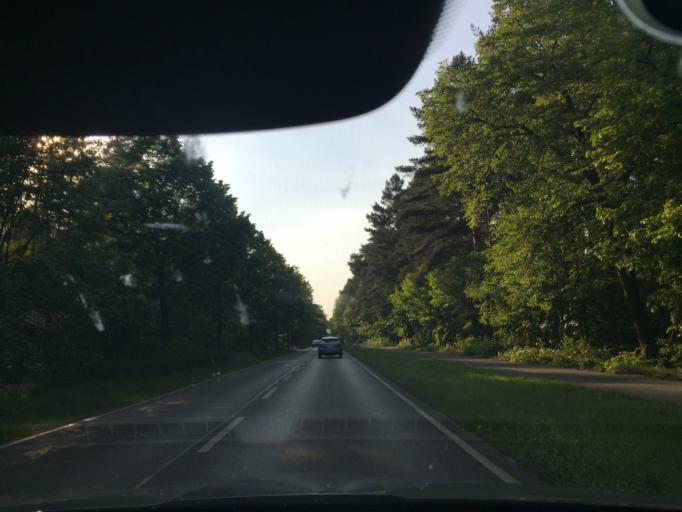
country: DE
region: Berlin
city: Grunau
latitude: 52.4030
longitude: 13.5948
